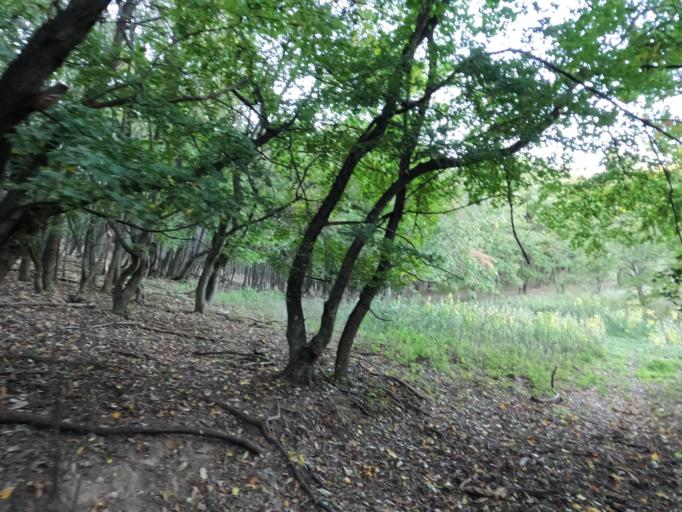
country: HU
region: Tolna
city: Szekszard
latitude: 46.3130
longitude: 18.6555
